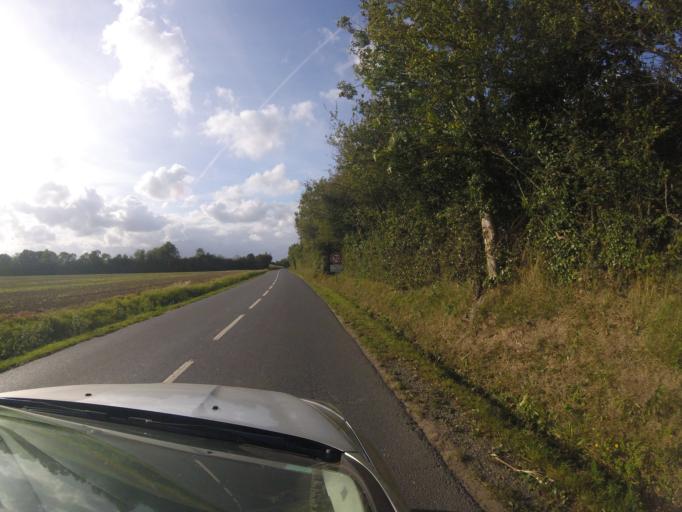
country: FR
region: Lower Normandy
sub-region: Departement du Calvados
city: Port-en-Bessin-Huppain
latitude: 49.3497
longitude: -0.8612
